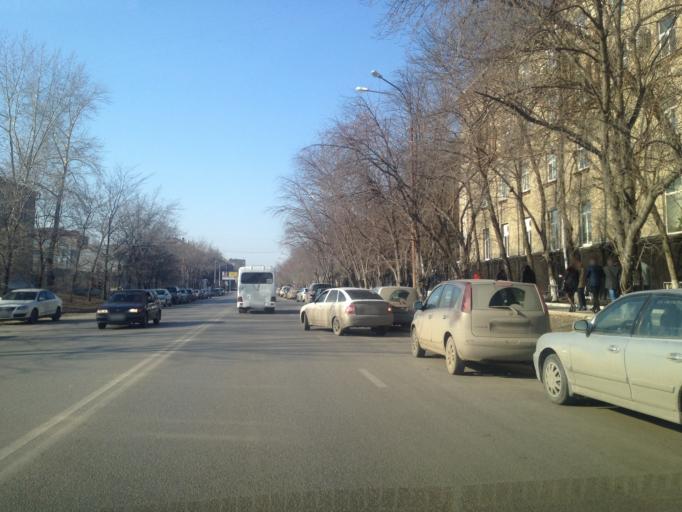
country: RU
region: Sverdlovsk
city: Yekaterinburg
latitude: 56.8494
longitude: 60.6565
